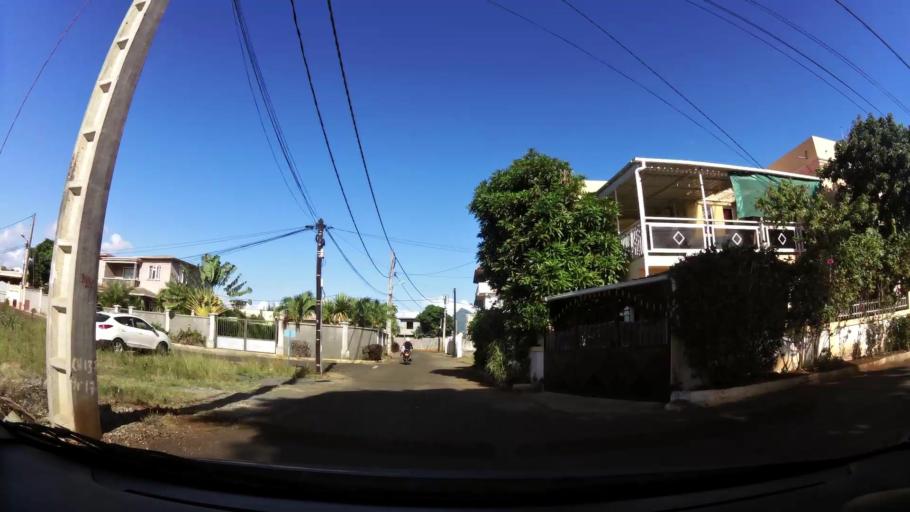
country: MU
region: Black River
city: Albion
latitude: -20.2002
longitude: 57.4111
